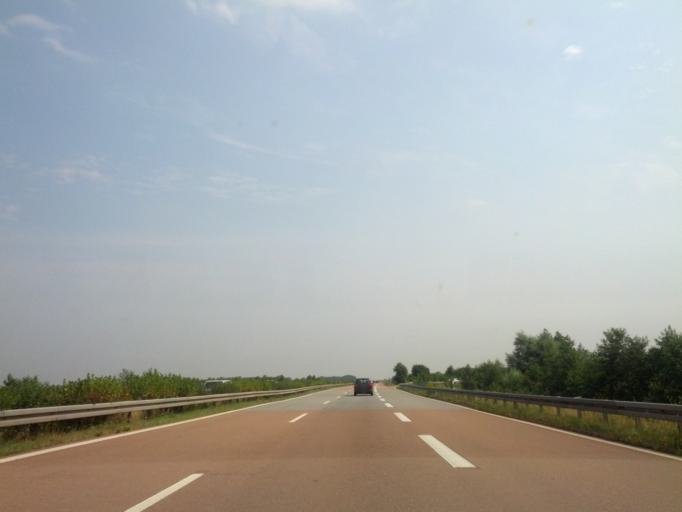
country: DE
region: Mecklenburg-Vorpommern
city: Tessin
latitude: 54.0395
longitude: 12.3634
